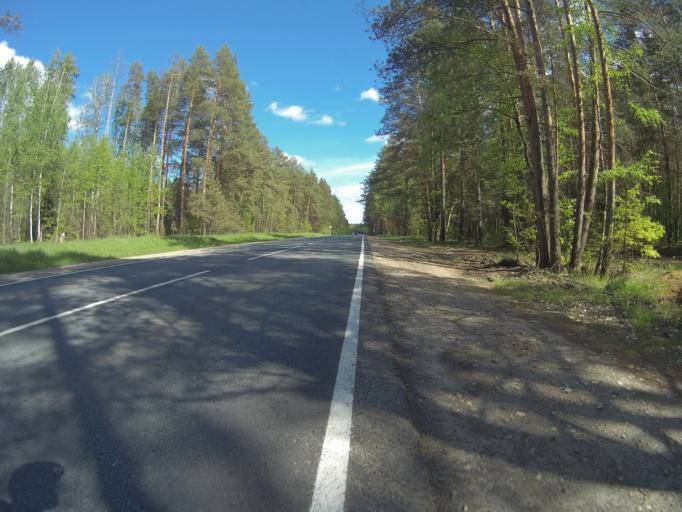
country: RU
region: Vladimir
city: Sudogda
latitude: 55.9729
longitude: 40.7870
